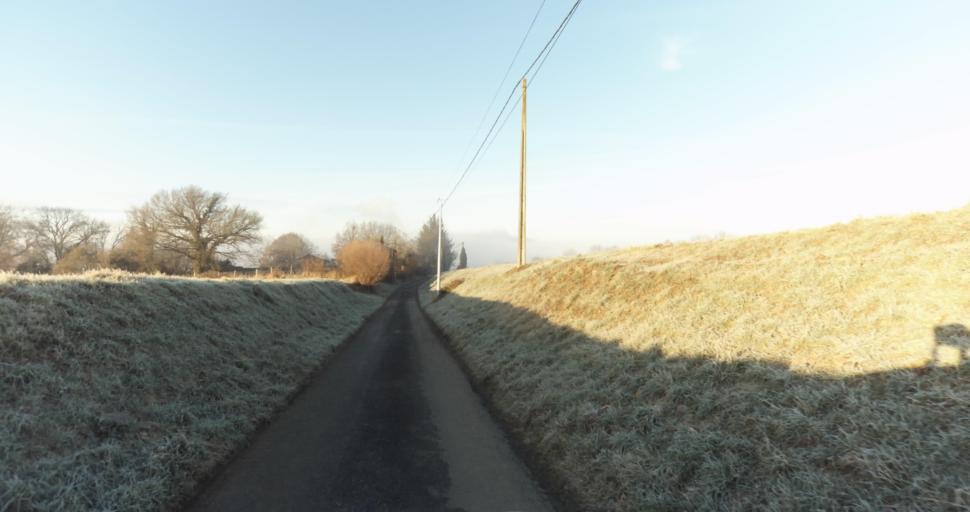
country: FR
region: Limousin
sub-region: Departement de la Haute-Vienne
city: Aixe-sur-Vienne
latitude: 45.7959
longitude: 1.1581
